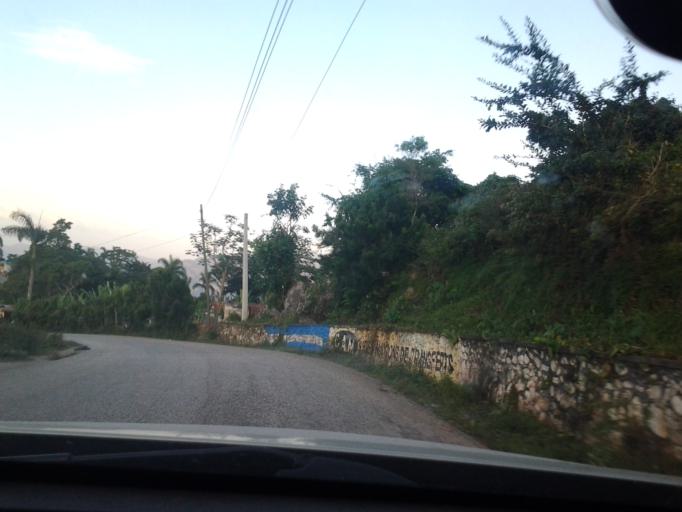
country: HT
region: Sud-Est
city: Jacmel
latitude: 18.3686
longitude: -72.5845
